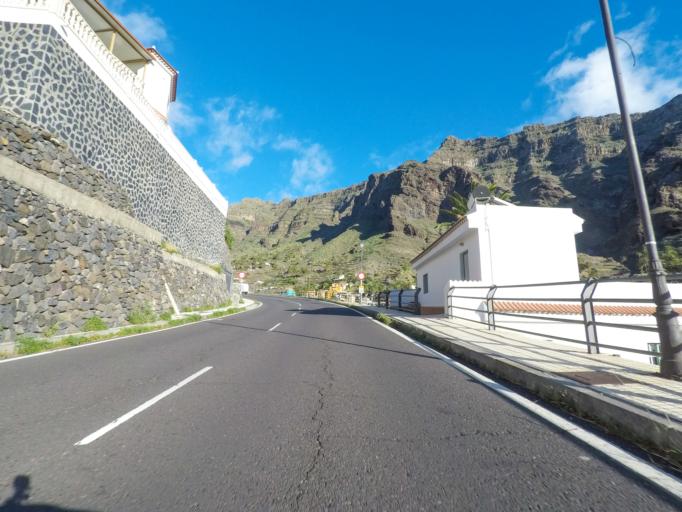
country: ES
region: Canary Islands
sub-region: Provincia de Santa Cruz de Tenerife
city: Vallehermosa
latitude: 28.1125
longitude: -17.3160
